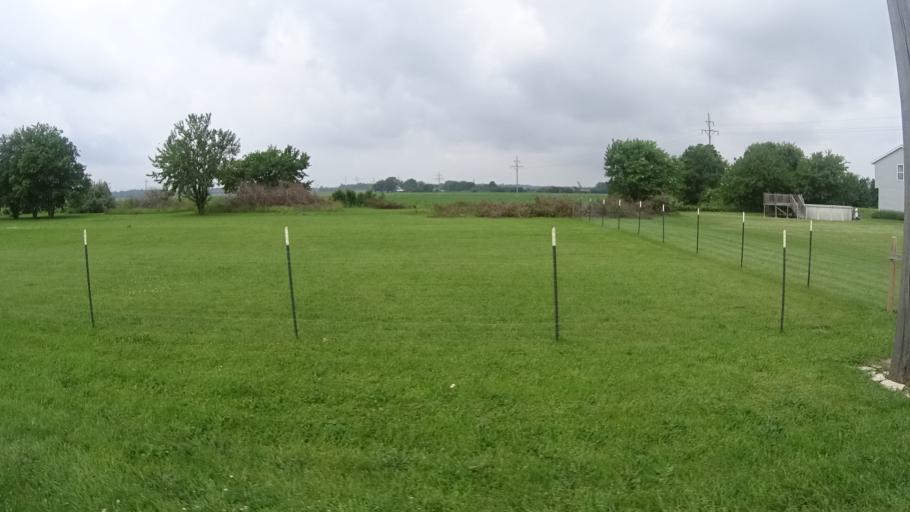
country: US
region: Ohio
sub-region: Huron County
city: Bellevue
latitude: 41.3438
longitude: -82.7941
